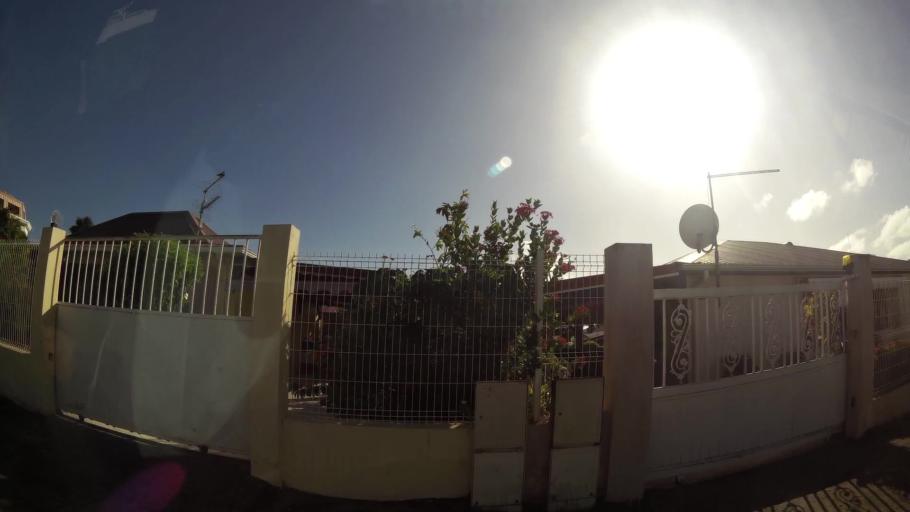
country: MQ
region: Martinique
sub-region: Martinique
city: Le Francois
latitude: 14.6206
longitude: -60.9010
